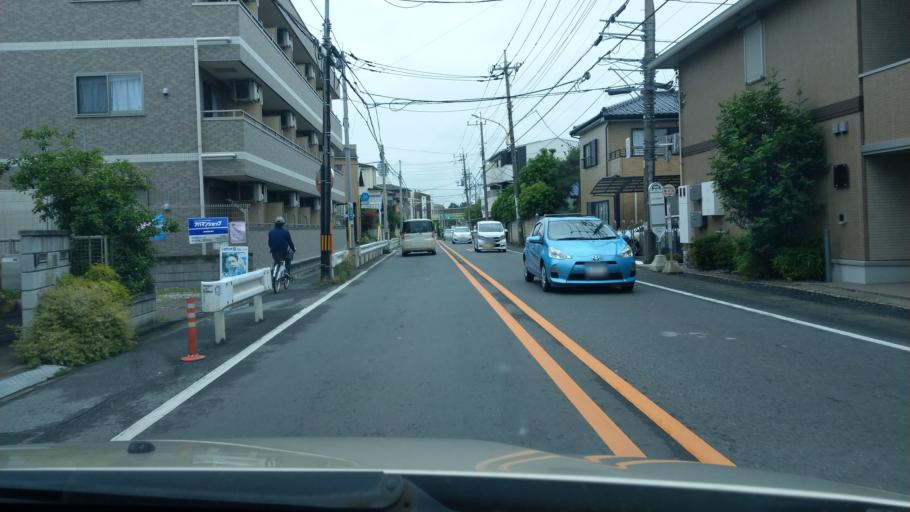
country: JP
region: Saitama
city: Saitama
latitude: 35.9122
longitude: 139.6339
